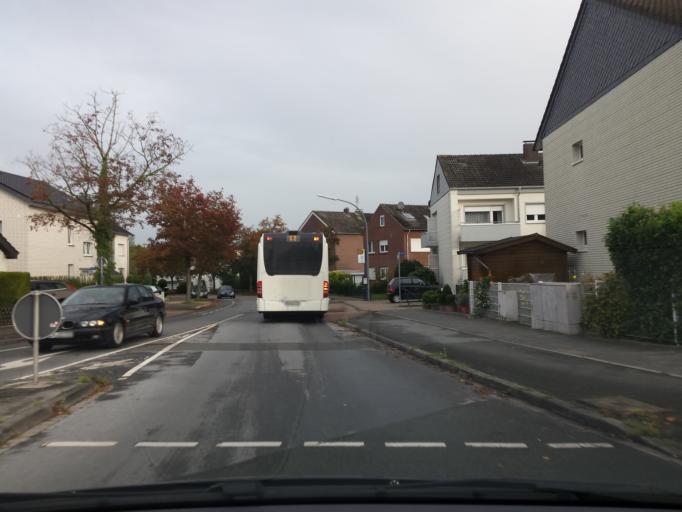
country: DE
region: North Rhine-Westphalia
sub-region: Regierungsbezirk Arnsberg
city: Lippstadt
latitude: 51.6607
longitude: 8.3286
